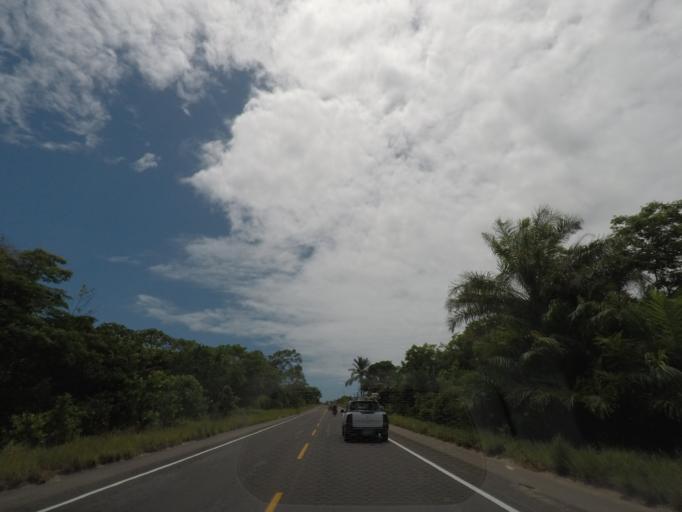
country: BR
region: Bahia
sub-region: Itaparica
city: Itaparica
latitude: -12.9716
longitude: -38.6356
